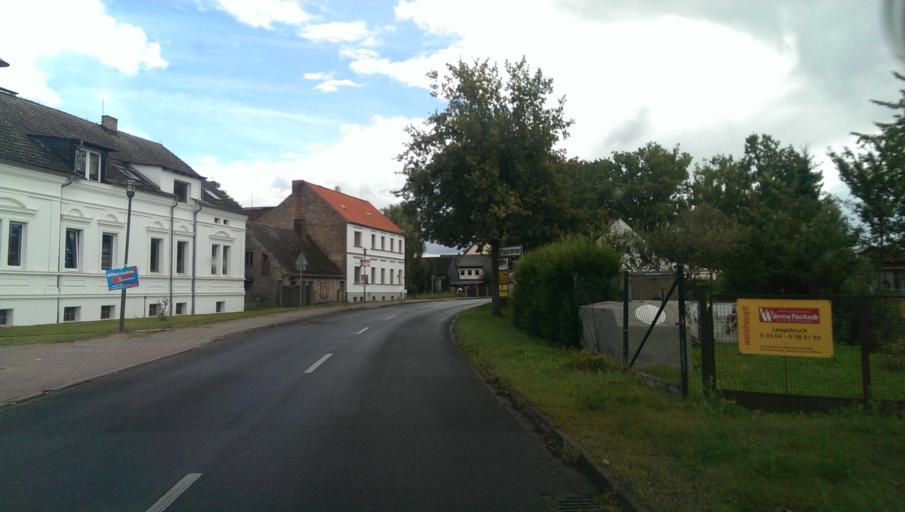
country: DE
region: Brandenburg
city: Velten
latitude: 52.6992
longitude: 13.1093
